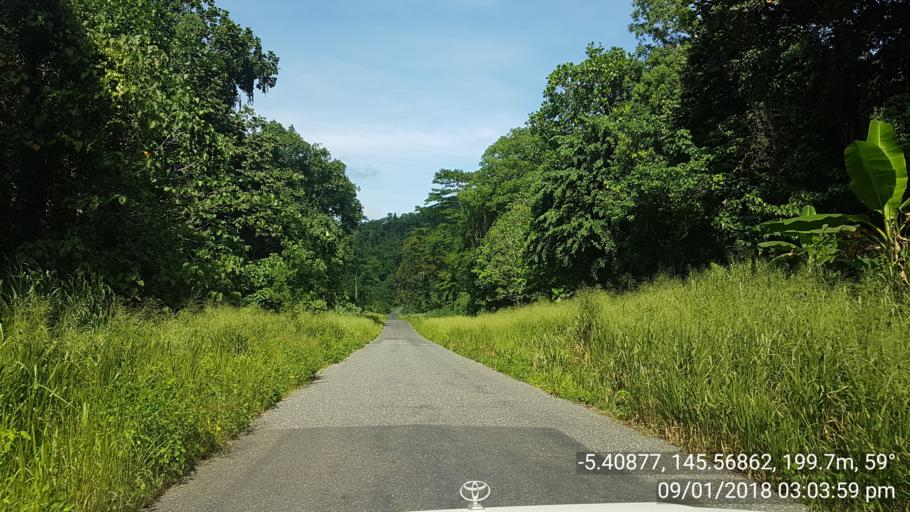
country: PG
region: Madang
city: Madang
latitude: -5.4089
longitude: 145.5686
